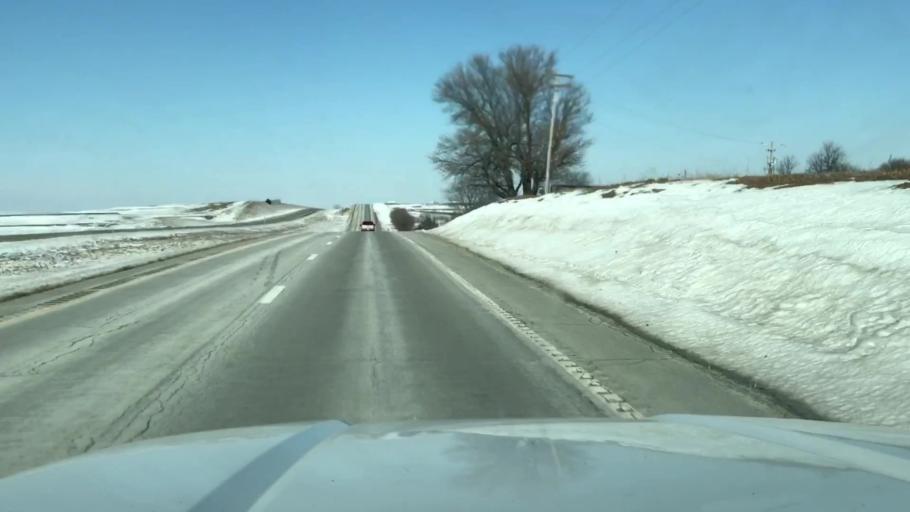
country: US
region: Missouri
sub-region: Andrew County
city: Savannah
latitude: 39.9688
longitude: -94.8690
